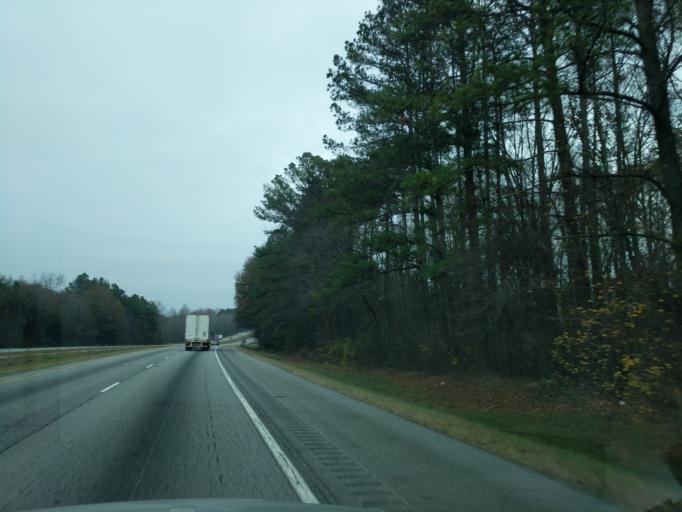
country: US
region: Georgia
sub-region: Franklin County
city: Carnesville
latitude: 34.3817
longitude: -83.2478
